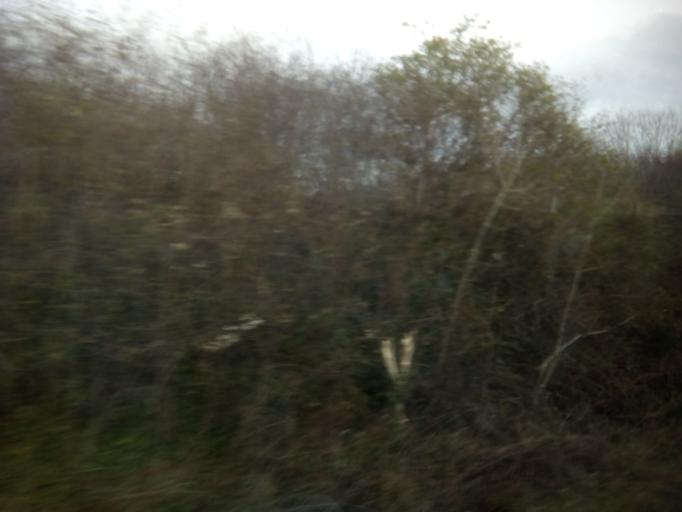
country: IE
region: Leinster
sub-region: Kildare
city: Kilcock
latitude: 53.4085
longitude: -6.6849
